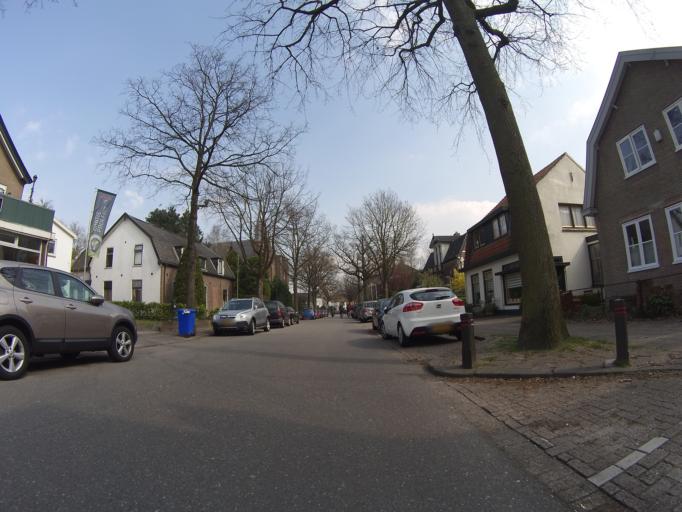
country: NL
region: Utrecht
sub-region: Gemeente Baarn
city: Baarn
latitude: 52.2138
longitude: 5.2934
